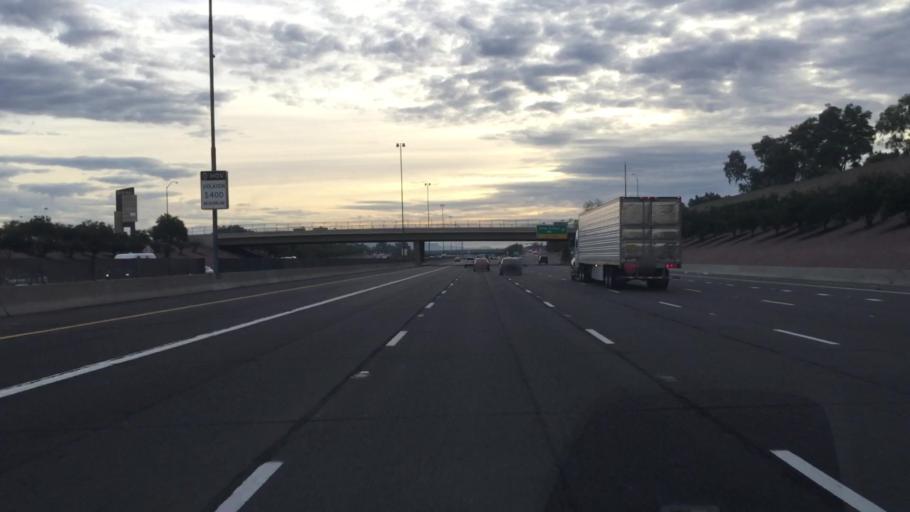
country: US
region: Arizona
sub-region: Maricopa County
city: Tempe
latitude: 33.3947
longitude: -111.8725
